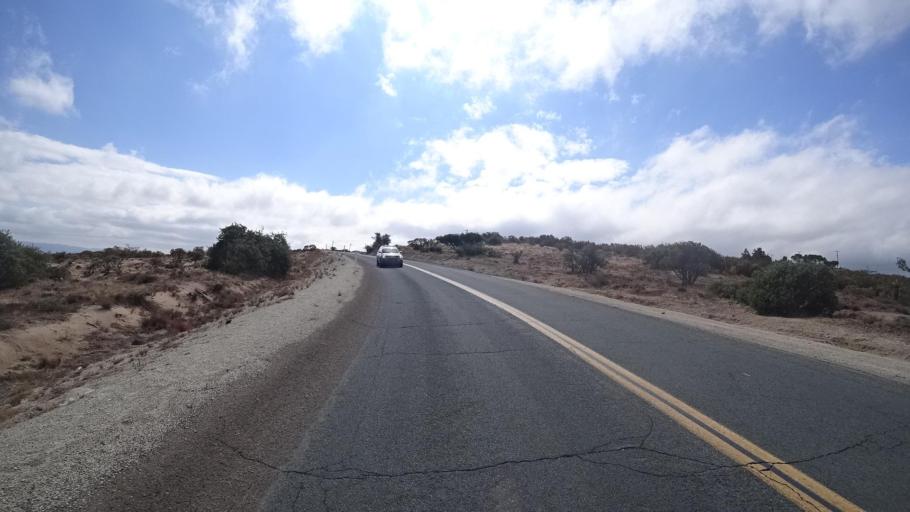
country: US
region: California
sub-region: San Diego County
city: Campo
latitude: 32.6607
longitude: -116.3166
